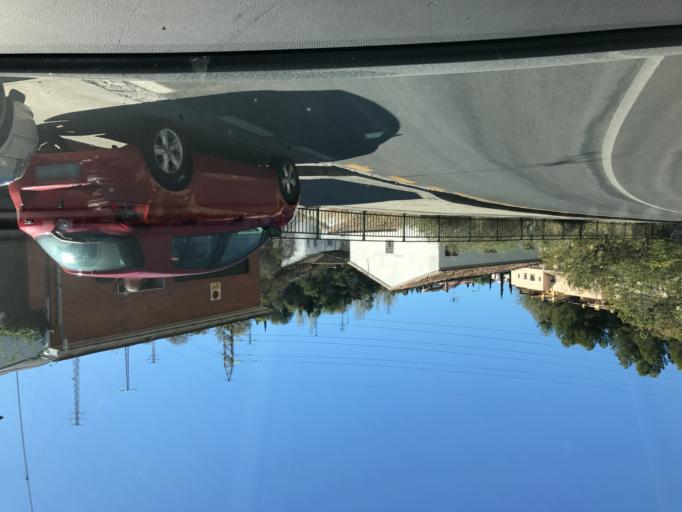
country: ES
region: Andalusia
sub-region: Provincia de Granada
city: Granada
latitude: 37.1862
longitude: -3.5992
